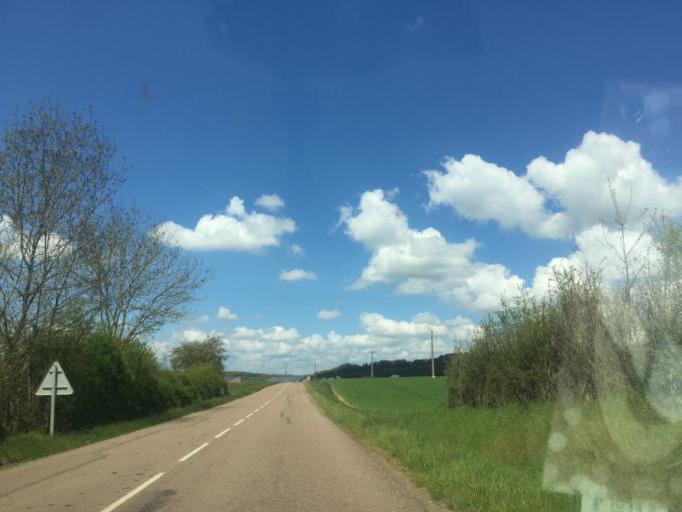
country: FR
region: Bourgogne
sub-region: Departement de l'Yonne
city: Fontenailles
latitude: 47.4753
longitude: 3.4375
